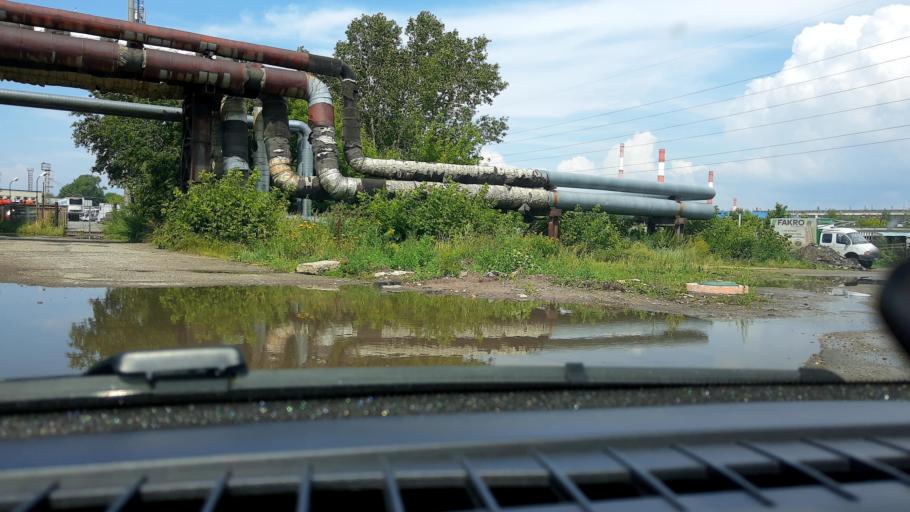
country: RU
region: Nizjnij Novgorod
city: Burevestnik
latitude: 56.2294
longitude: 43.8876
